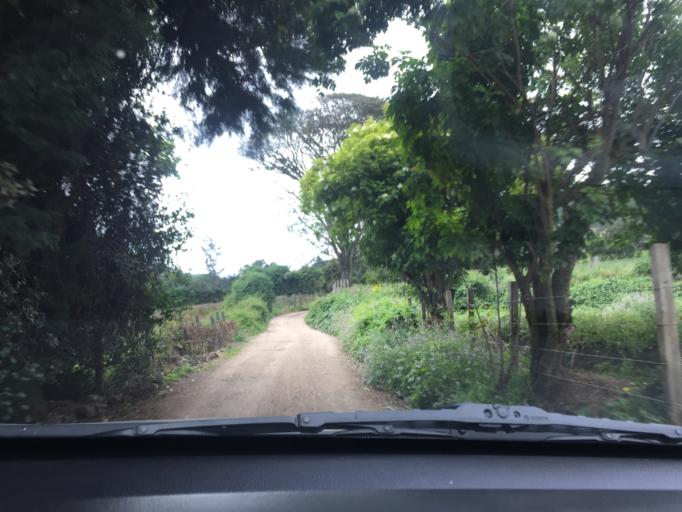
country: CO
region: Cundinamarca
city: Tabio
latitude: 4.9404
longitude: -74.1287
